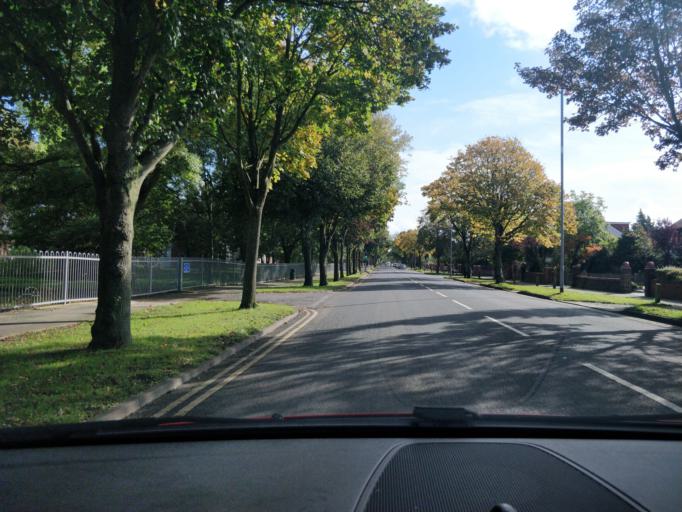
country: GB
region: England
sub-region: Sefton
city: Southport
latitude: 53.6365
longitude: -2.9811
